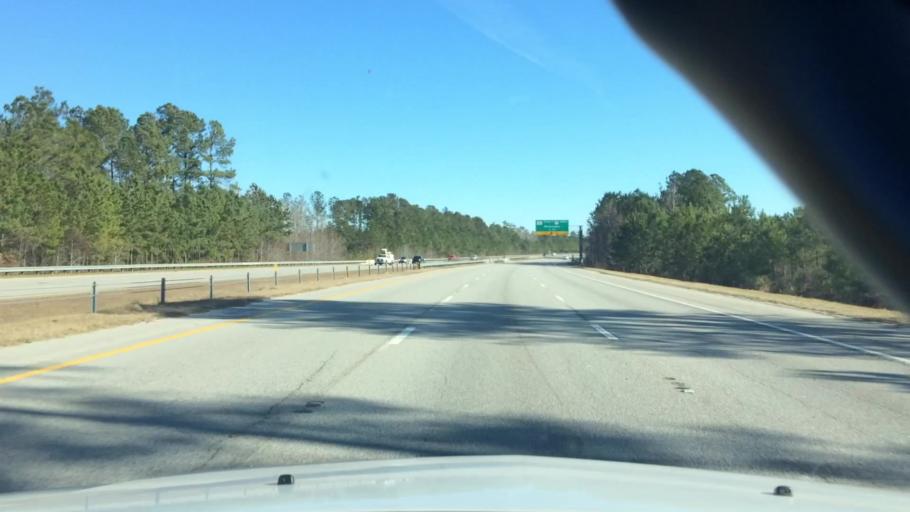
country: US
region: South Carolina
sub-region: Horry County
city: North Myrtle Beach
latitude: 33.8670
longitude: -78.6924
